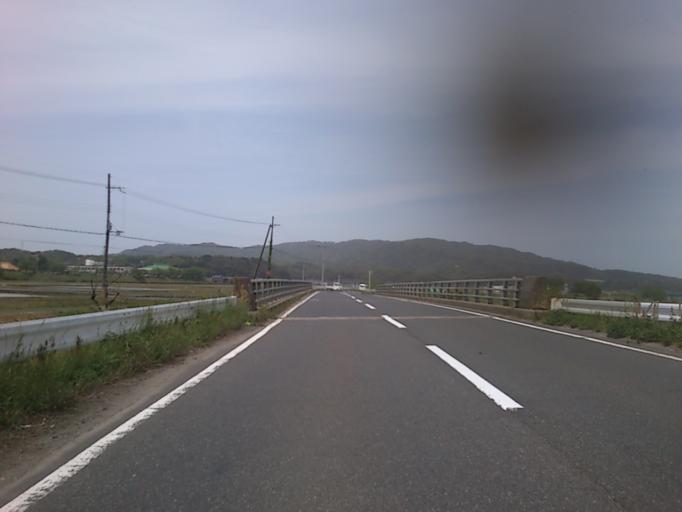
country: JP
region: Kyoto
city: Miyazu
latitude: 35.6636
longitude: 135.0862
